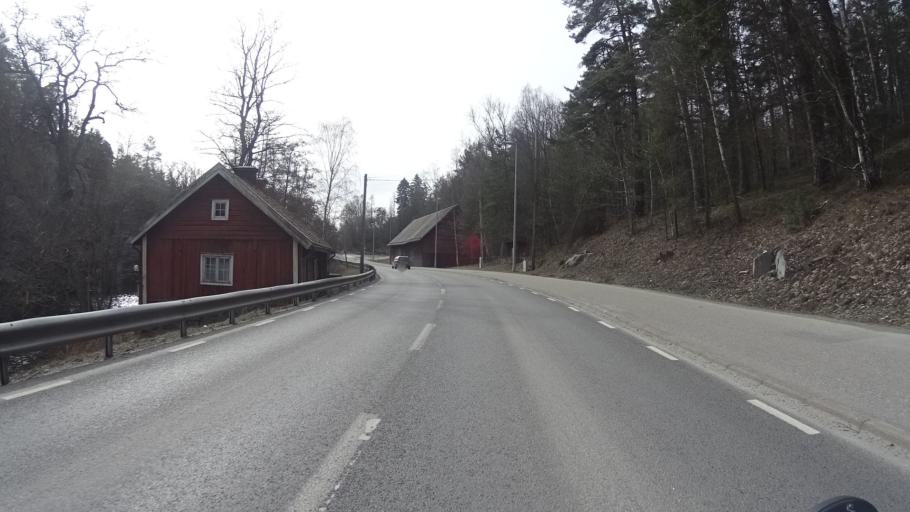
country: SE
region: Stockholm
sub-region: Nacka Kommun
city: Nacka
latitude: 59.2974
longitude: 18.1458
